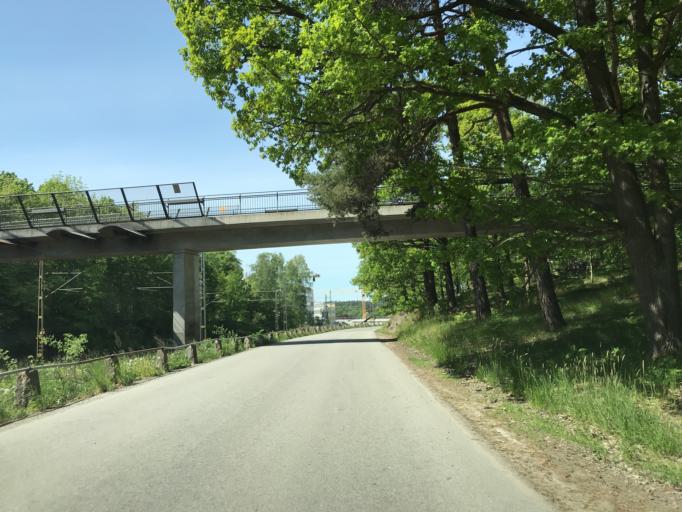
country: SE
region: Stockholm
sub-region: Stockholms Kommun
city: Stockholm
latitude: 59.3528
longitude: 18.0631
